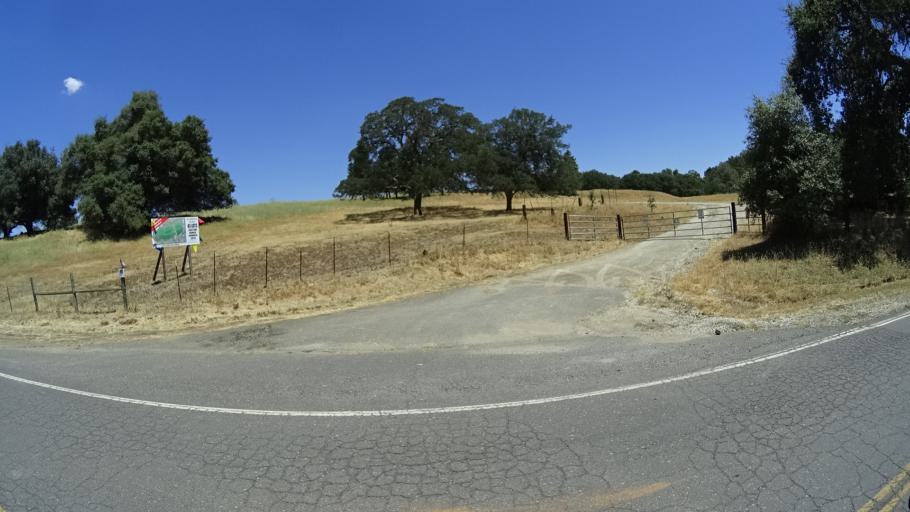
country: US
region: California
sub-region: Calaveras County
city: Murphys
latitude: 38.1229
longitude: -120.4655
